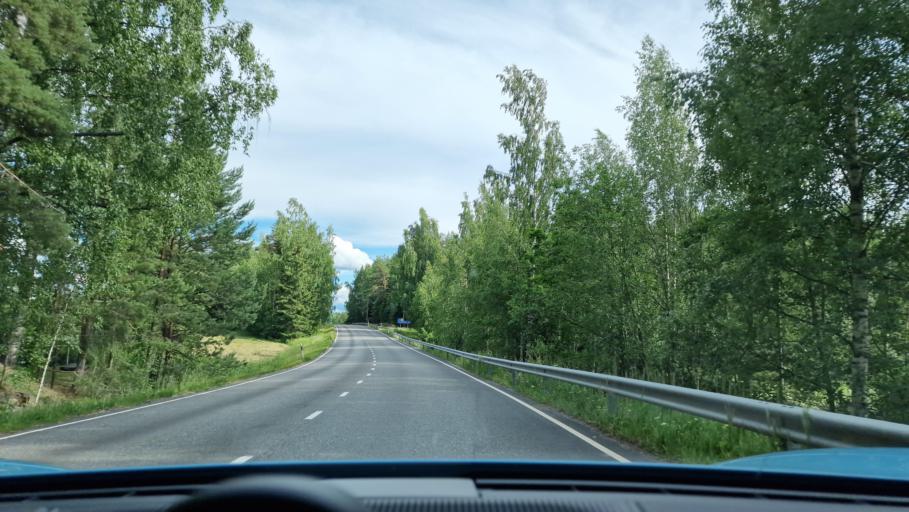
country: FI
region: Pirkanmaa
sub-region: Tampere
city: Sahalahti
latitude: 61.5576
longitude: 24.3082
